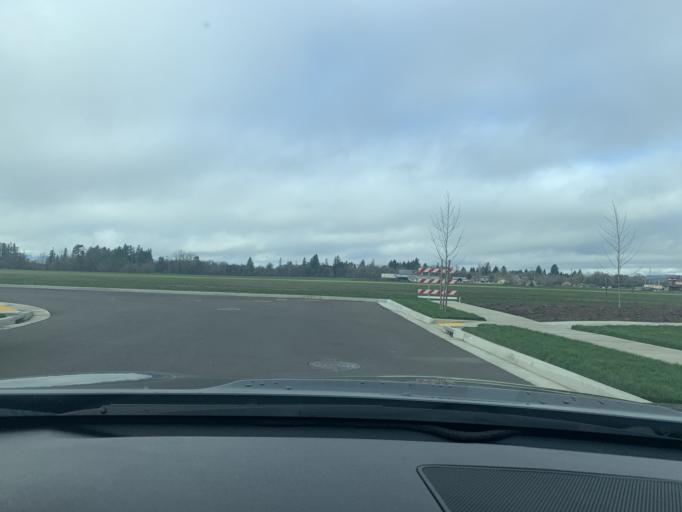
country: US
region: Oregon
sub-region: Washington County
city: North Plains
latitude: 45.5944
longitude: -122.9789
